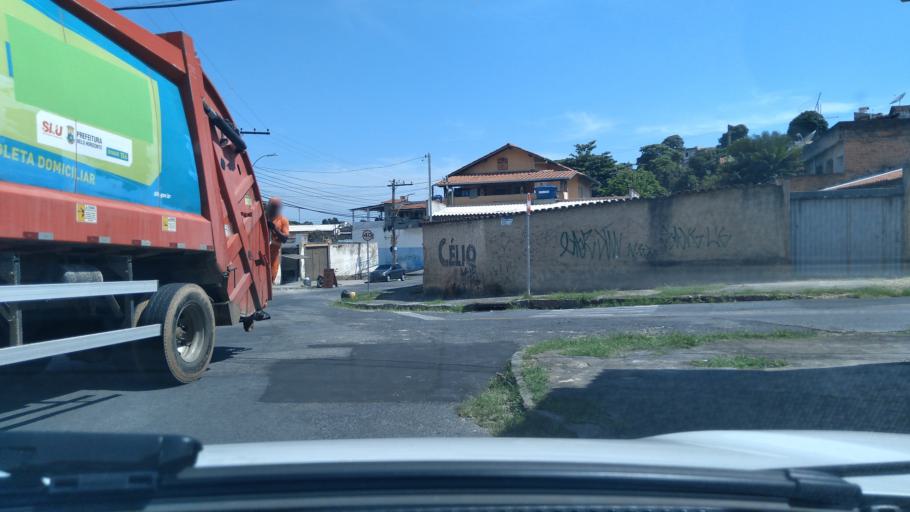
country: BR
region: Minas Gerais
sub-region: Contagem
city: Contagem
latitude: -19.9186
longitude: -44.0046
